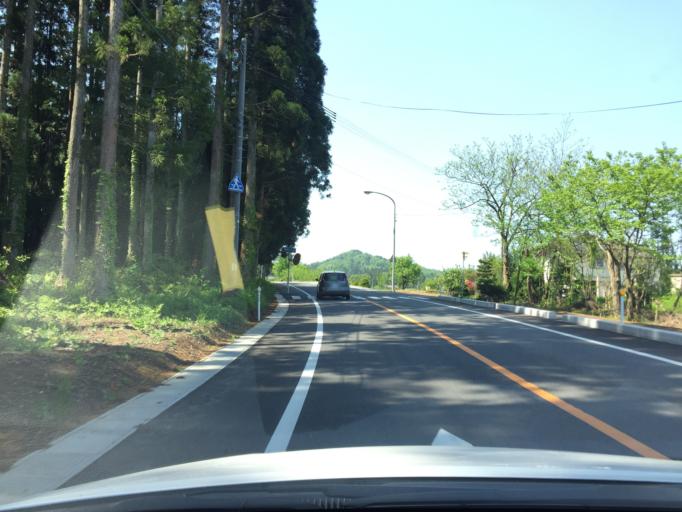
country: JP
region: Niigata
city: Muramatsu
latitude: 37.6648
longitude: 139.1388
